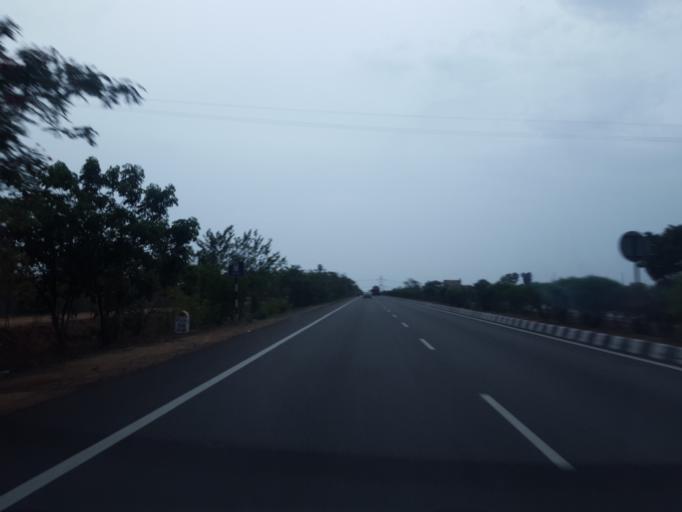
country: IN
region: Telangana
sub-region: Mahbubnagar
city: Farrukhnagar
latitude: 17.0921
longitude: 78.2417
